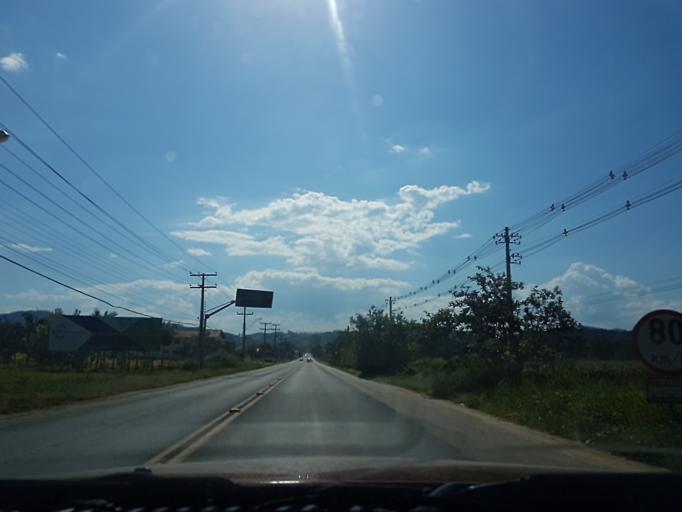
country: BR
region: Santa Catarina
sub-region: Braco Do Norte
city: Braco do Norte
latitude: -28.3231
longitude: -49.1602
